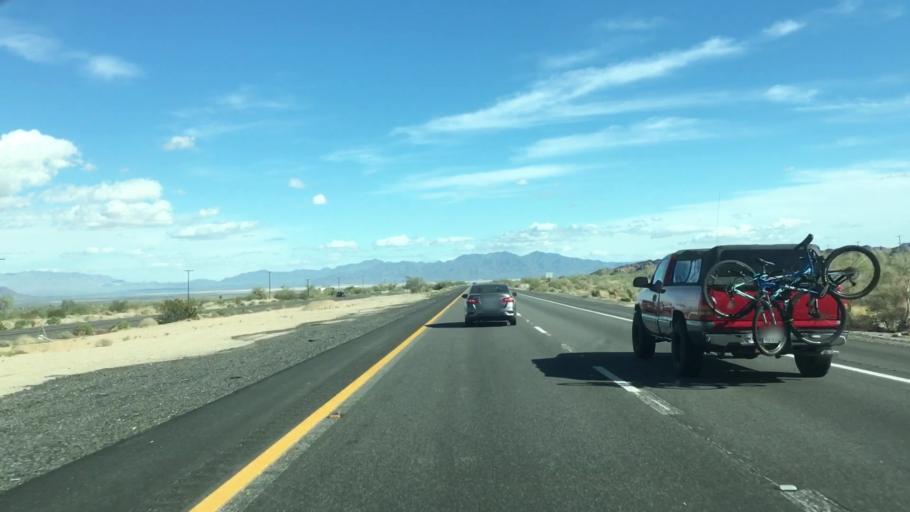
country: US
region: California
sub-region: Imperial County
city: Niland
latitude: 33.7032
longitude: -115.4473
